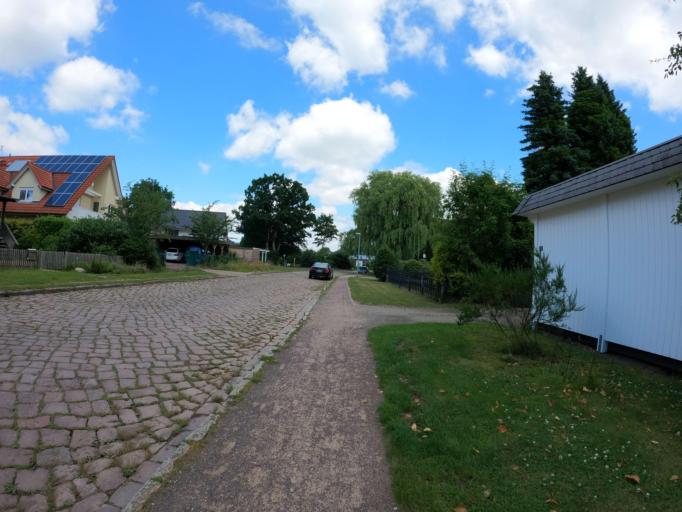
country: DE
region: Schleswig-Holstein
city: Bornsen
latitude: 53.4936
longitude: 10.2680
